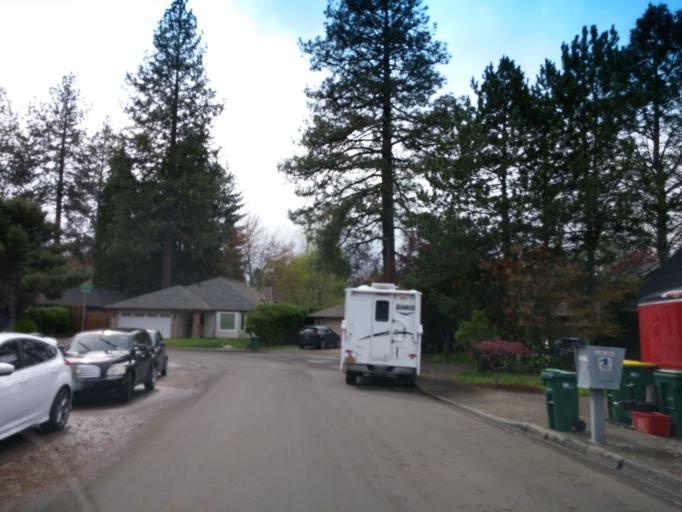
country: US
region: Oregon
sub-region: Washington County
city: Cedar Mill
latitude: 45.5185
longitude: -122.8298
